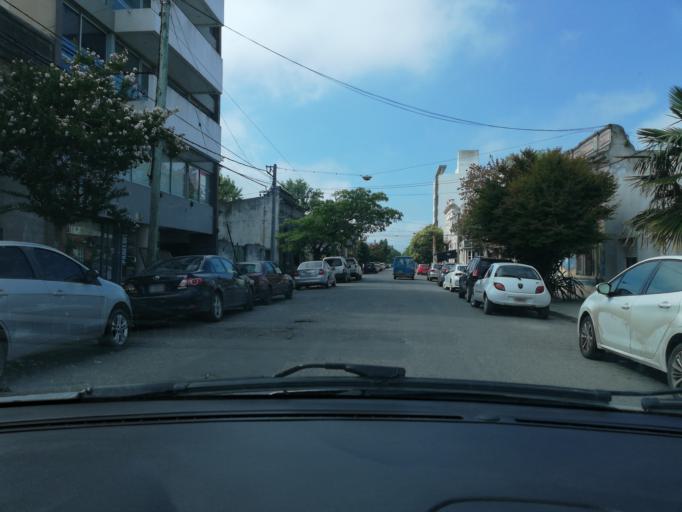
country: AR
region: Buenos Aires
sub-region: Partido de Balcarce
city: Balcarce
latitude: -37.8453
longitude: -58.2530
